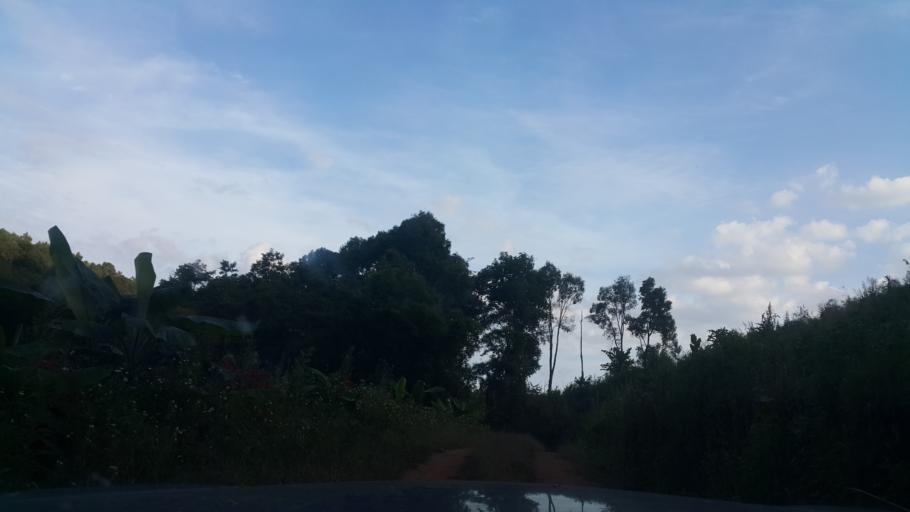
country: TH
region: Chiang Mai
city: Samoeng
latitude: 19.0185
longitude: 98.6502
